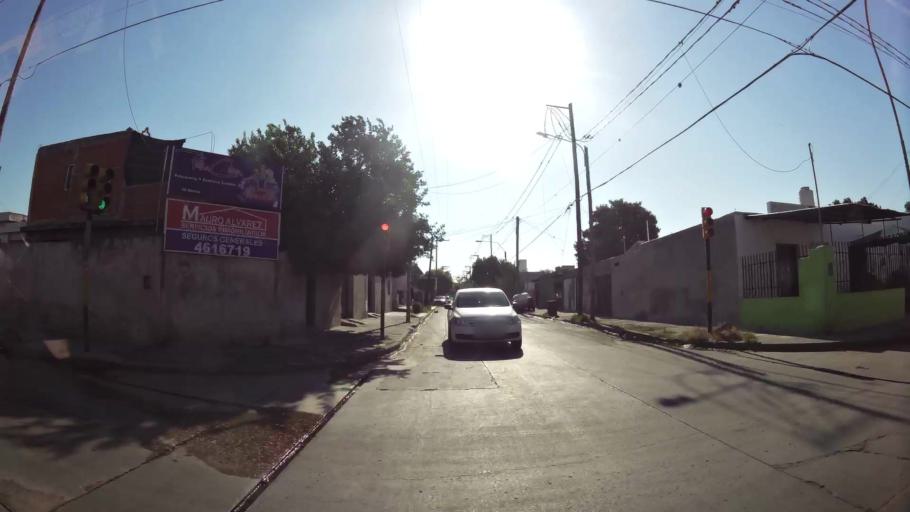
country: AR
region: Cordoba
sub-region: Departamento de Capital
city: Cordoba
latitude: -31.4722
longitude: -64.2246
